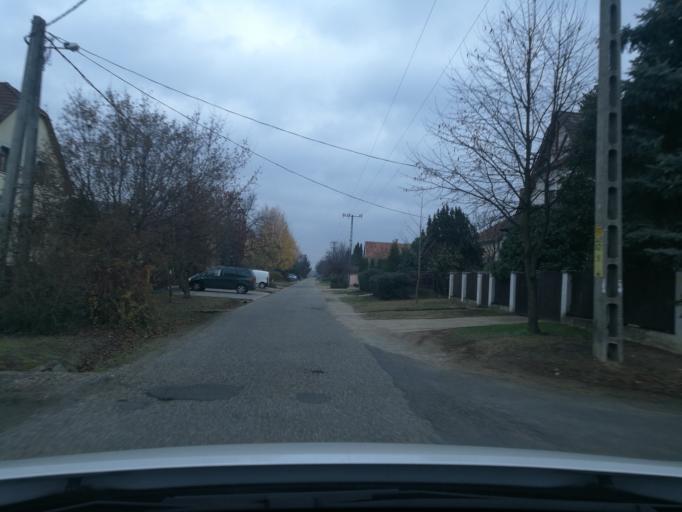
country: HU
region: Szabolcs-Szatmar-Bereg
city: Nyirpazony
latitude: 47.9566
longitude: 21.7765
